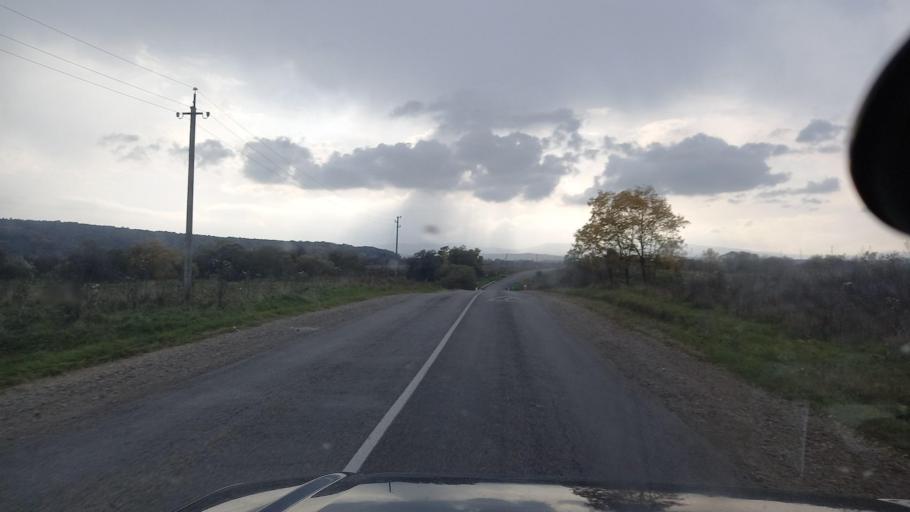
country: RU
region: Krasnodarskiy
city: Gubskaya
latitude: 44.3525
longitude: 40.6982
